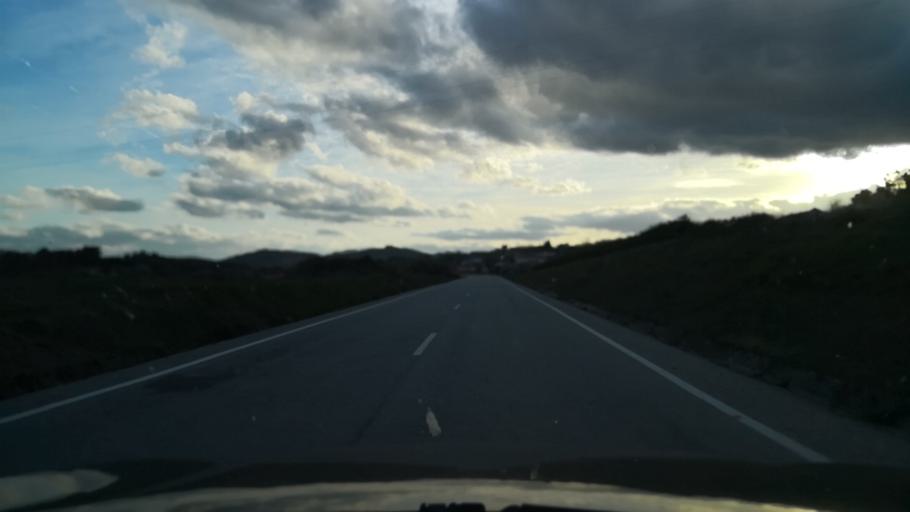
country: PT
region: Braganca
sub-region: Carrazeda de Ansiaes
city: Carrazeda de Anciaes
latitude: 41.2391
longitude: -7.3213
